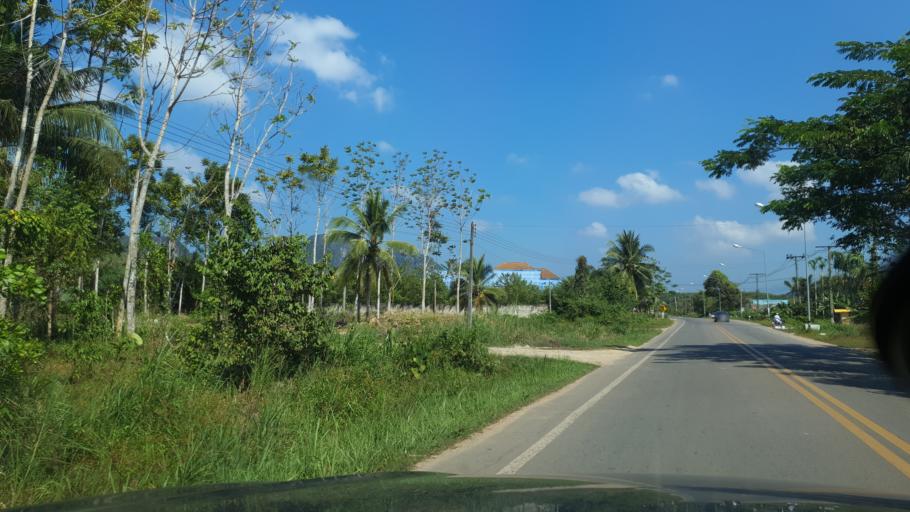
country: TH
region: Phangnga
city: Ban Ao Nang
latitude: 8.0580
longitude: 98.8588
